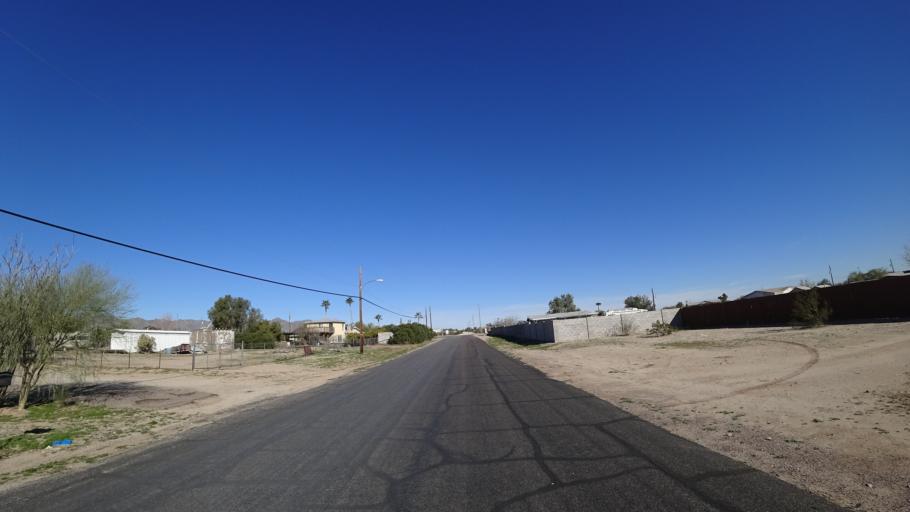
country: US
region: Arizona
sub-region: Maricopa County
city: Citrus Park
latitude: 33.4707
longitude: -112.4875
